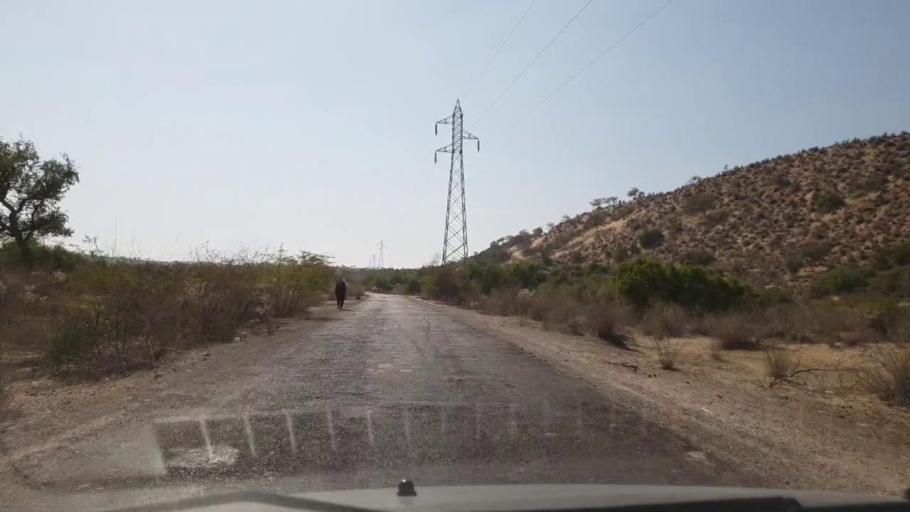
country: PK
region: Sindh
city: Mithi
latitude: 24.6408
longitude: 69.7445
